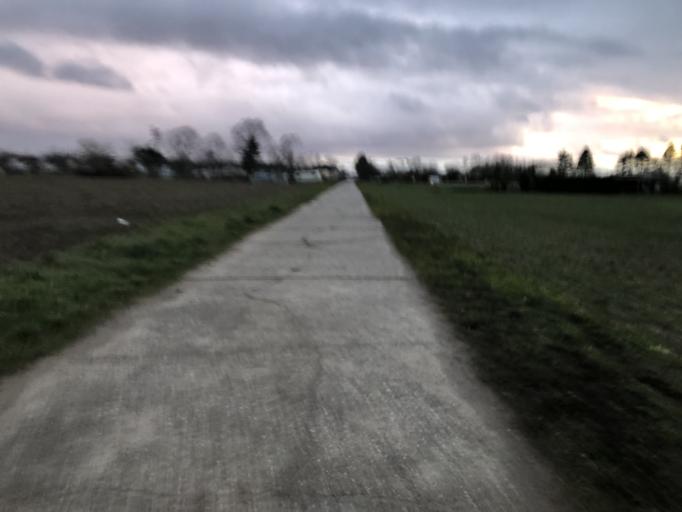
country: DE
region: Baden-Wuerttemberg
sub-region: Karlsruhe Region
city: Neulussheim
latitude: 49.3023
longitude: 8.5197
